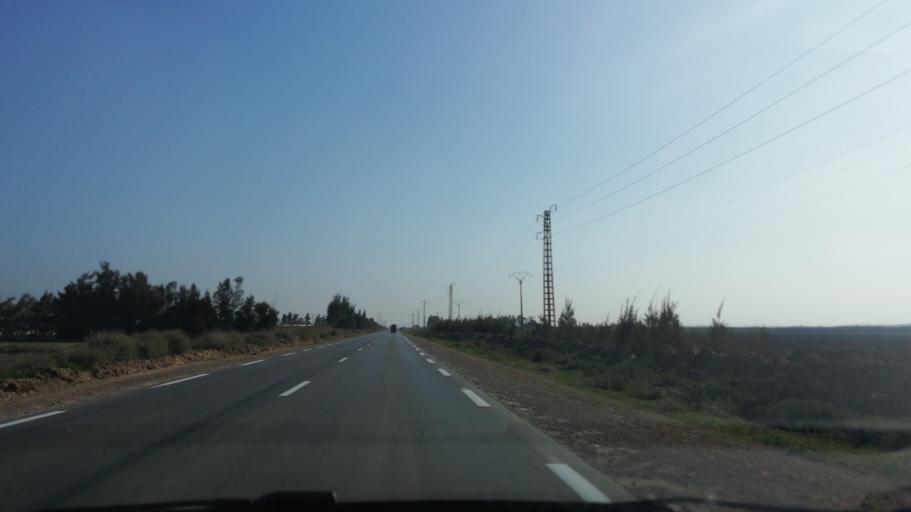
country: DZ
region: Mostaganem
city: Mostaganem
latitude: 35.7452
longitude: 0.0175
